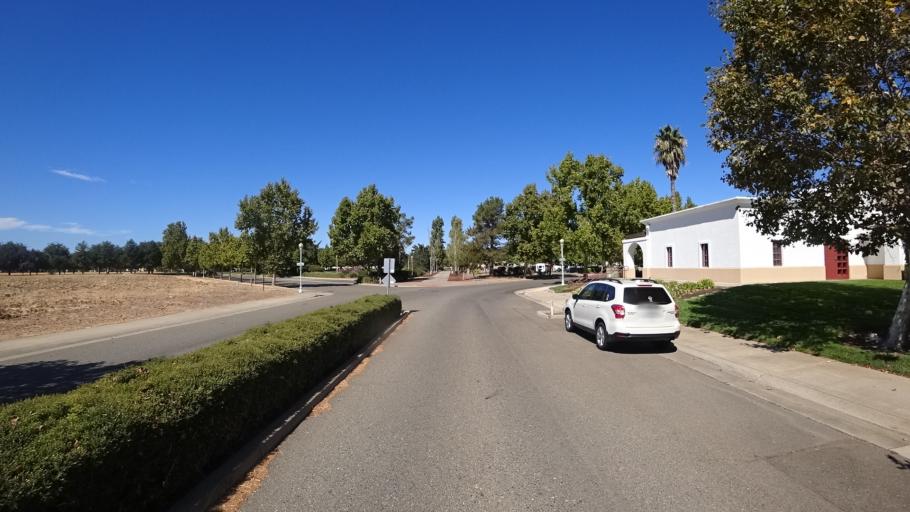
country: US
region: California
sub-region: Sacramento County
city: Laguna
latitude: 38.4241
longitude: -121.4684
